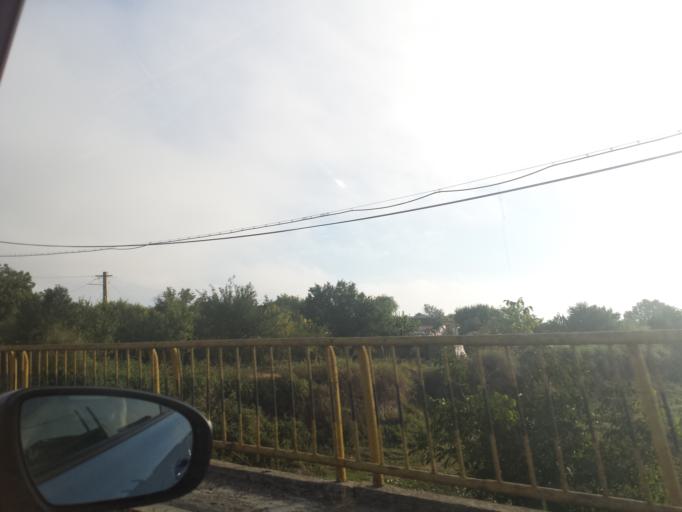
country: RO
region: Constanta
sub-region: Comuna Saraiu
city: Saraiu
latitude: 44.7198
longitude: 28.1563
